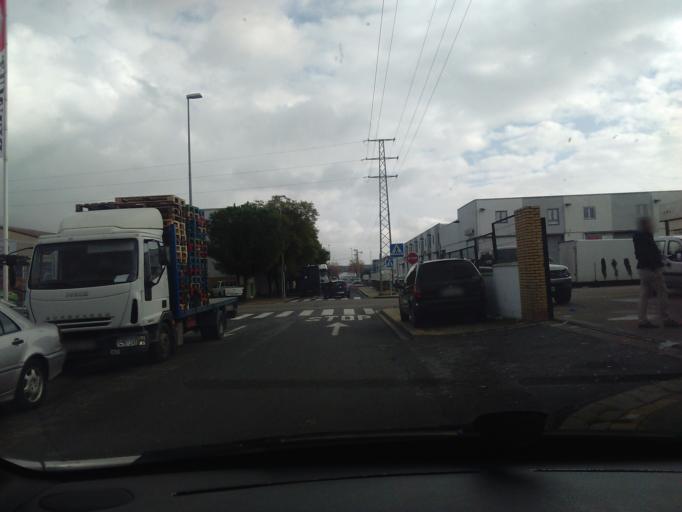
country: ES
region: Andalusia
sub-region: Provincia de Sevilla
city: Sevilla
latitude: 37.3749
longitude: -5.9277
